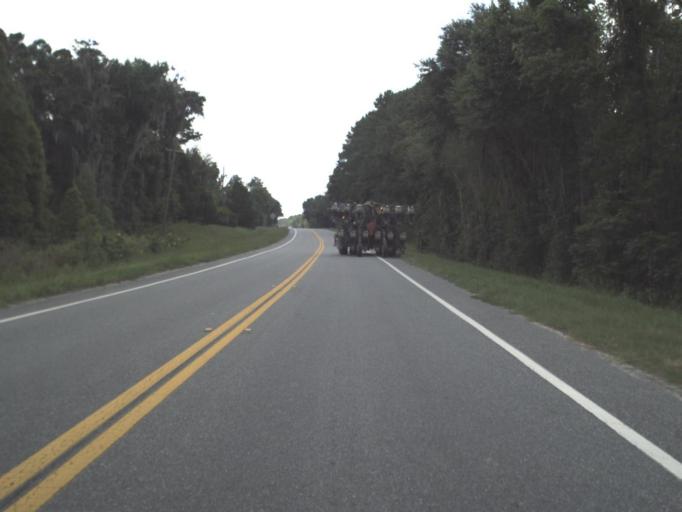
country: US
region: Florida
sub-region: Hamilton County
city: Jasper
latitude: 30.5341
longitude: -83.0456
